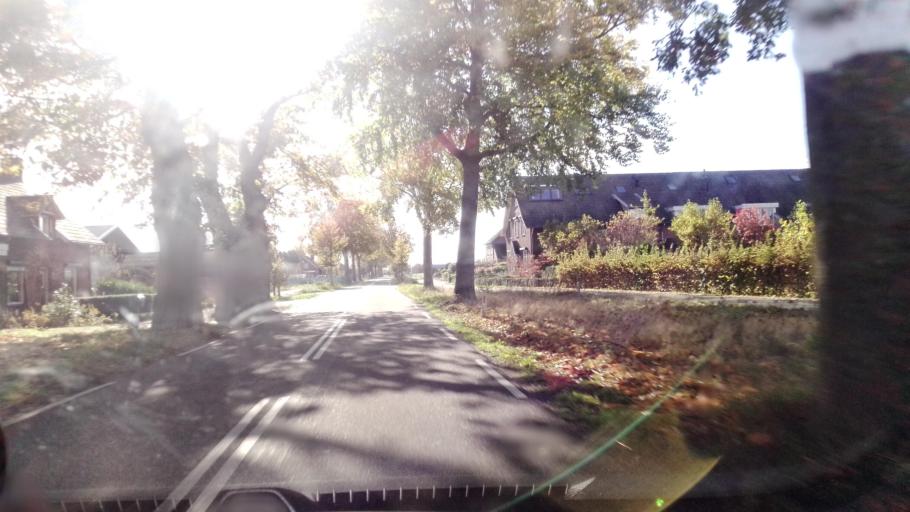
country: NL
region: Limburg
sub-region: Gemeente Venlo
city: Arcen
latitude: 51.4435
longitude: 6.1496
